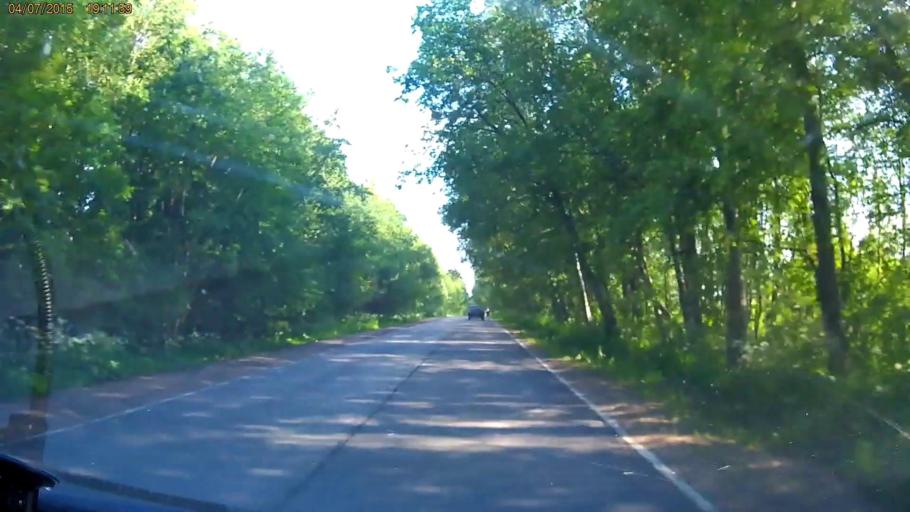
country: RU
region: Leningrad
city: Garbolovo
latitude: 60.3214
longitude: 30.4937
